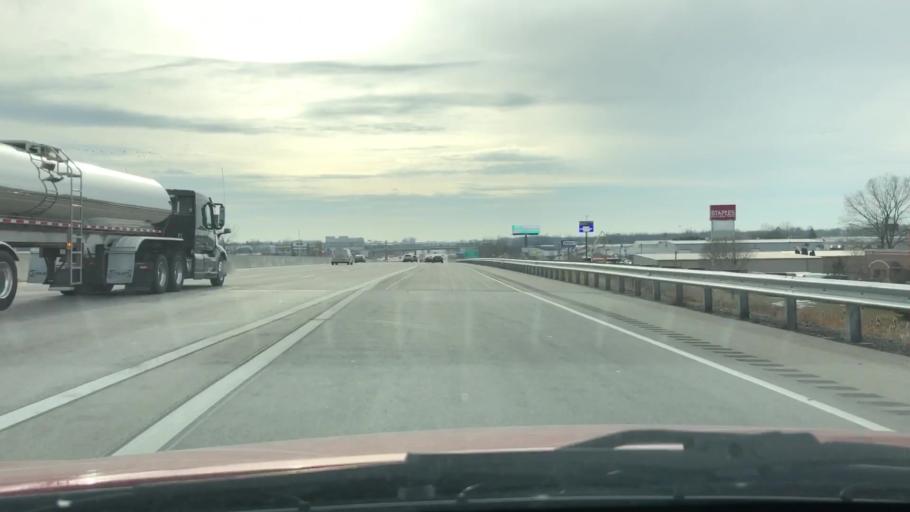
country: US
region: Wisconsin
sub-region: Brown County
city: Ashwaubenon
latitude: 44.4651
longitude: -88.0816
